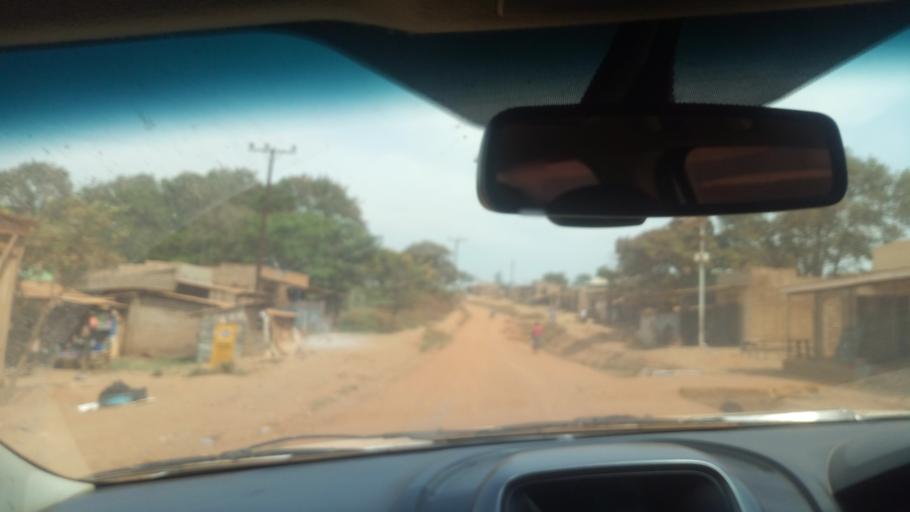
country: UG
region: Western Region
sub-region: Kiryandongo District
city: Kiryandongo
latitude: 1.9398
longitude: 32.1662
